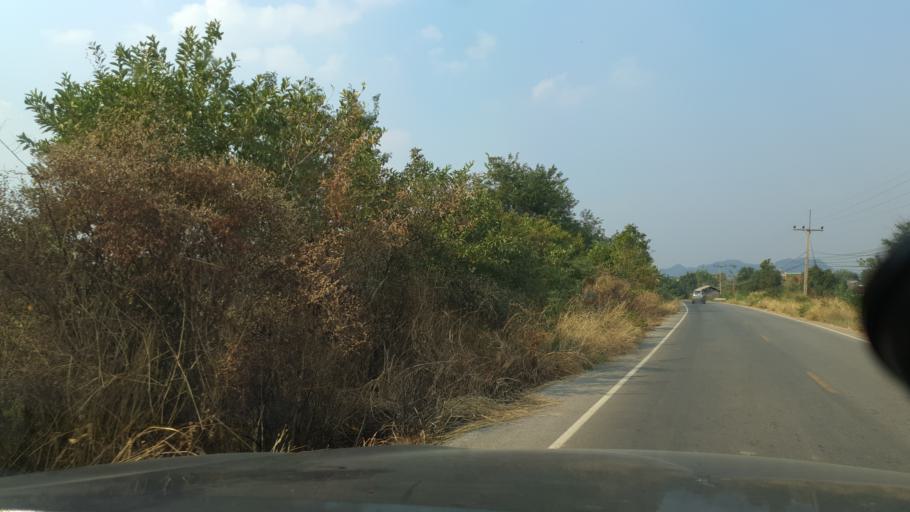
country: TH
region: Sukhothai
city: Ban Dan Lan Hoi
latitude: 17.1082
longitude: 99.5507
